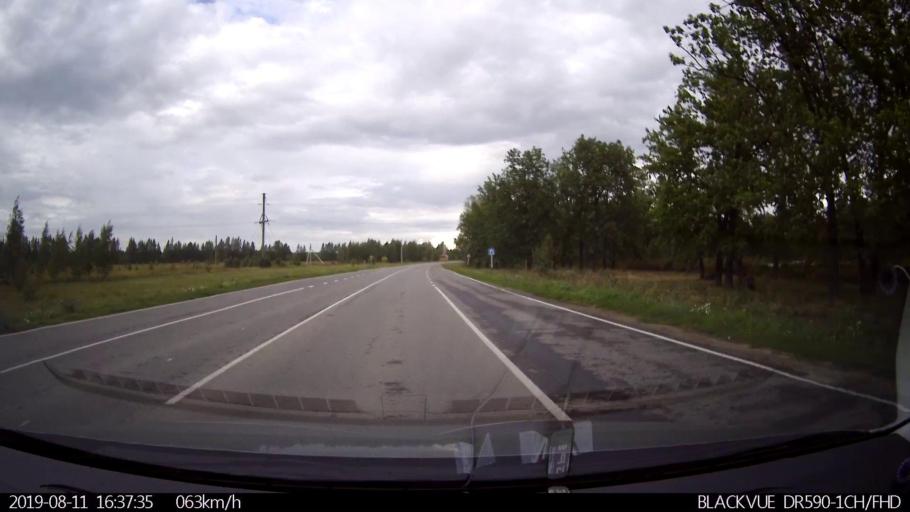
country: RU
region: Ulyanovsk
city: Mayna
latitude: 54.1286
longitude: 47.6154
